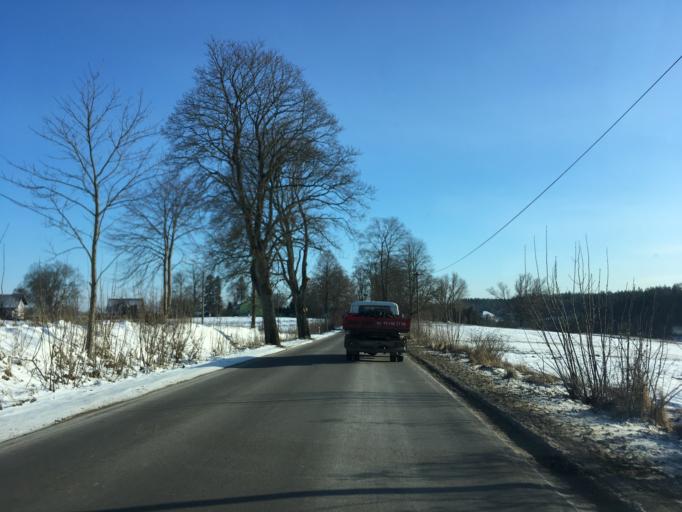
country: PL
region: Pomeranian Voivodeship
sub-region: Powiat koscierski
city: Koscierzyna
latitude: 54.0741
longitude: 18.0061
